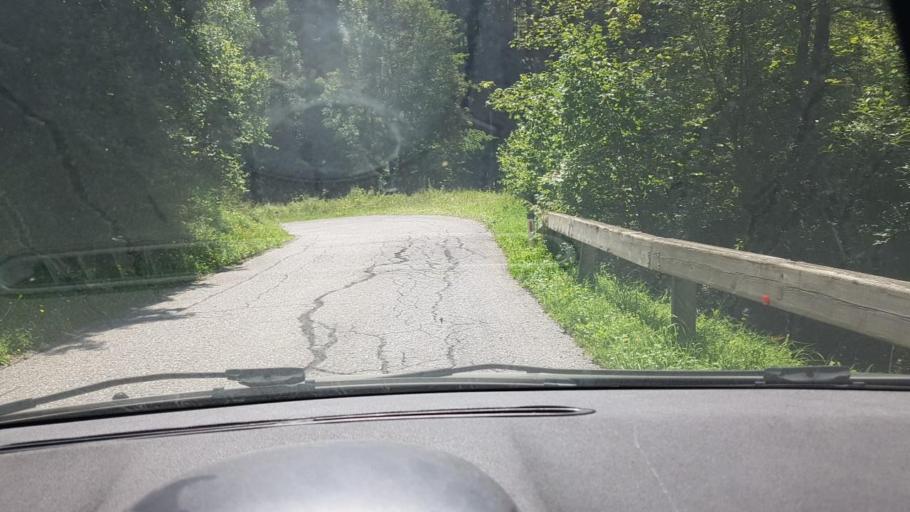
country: SI
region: Jezersko
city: Zgornje Jezersko
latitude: 46.4201
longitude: 14.5510
